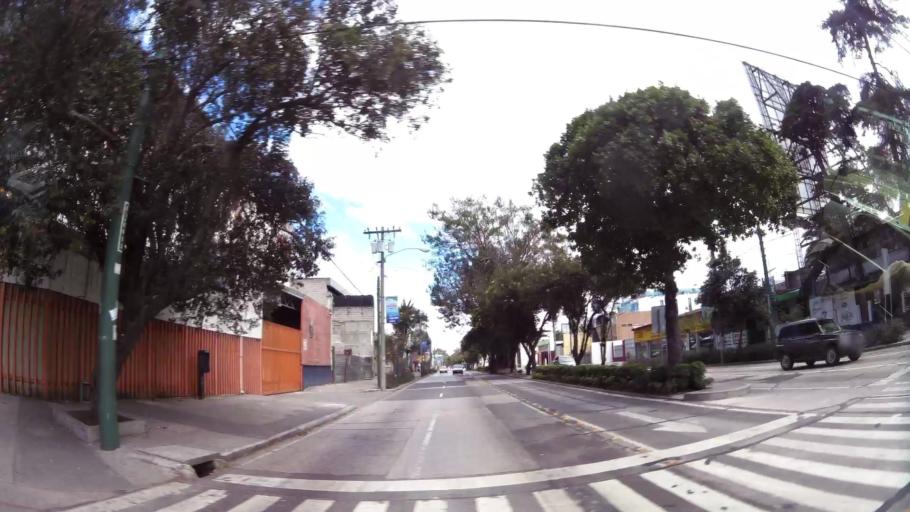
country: GT
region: Guatemala
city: Santa Catarina Pinula
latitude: 14.5986
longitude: -90.5212
